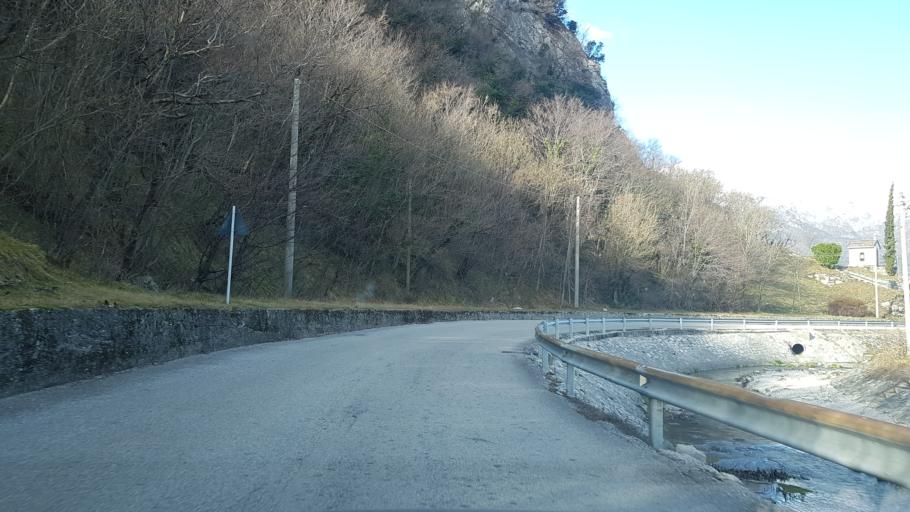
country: IT
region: Friuli Venezia Giulia
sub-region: Provincia di Udine
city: Trasaghis
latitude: 46.2882
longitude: 13.0538
